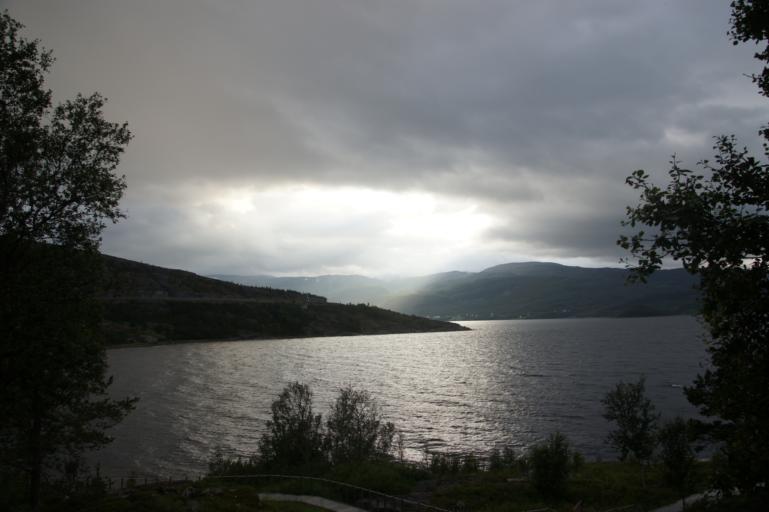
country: NO
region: Finnmark Fylke
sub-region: Alta
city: Alta
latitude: 69.9514
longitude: 23.1935
